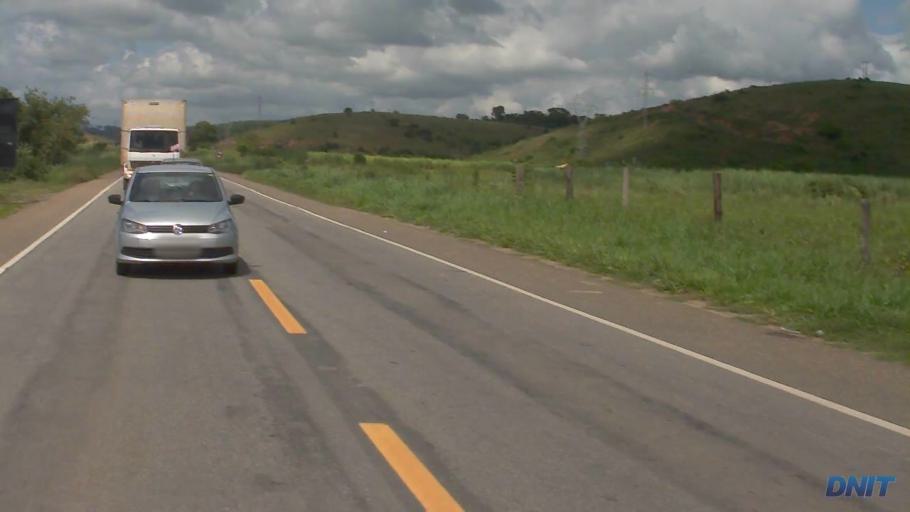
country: BR
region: Minas Gerais
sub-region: Governador Valadares
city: Governador Valadares
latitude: -19.0575
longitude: -42.1602
